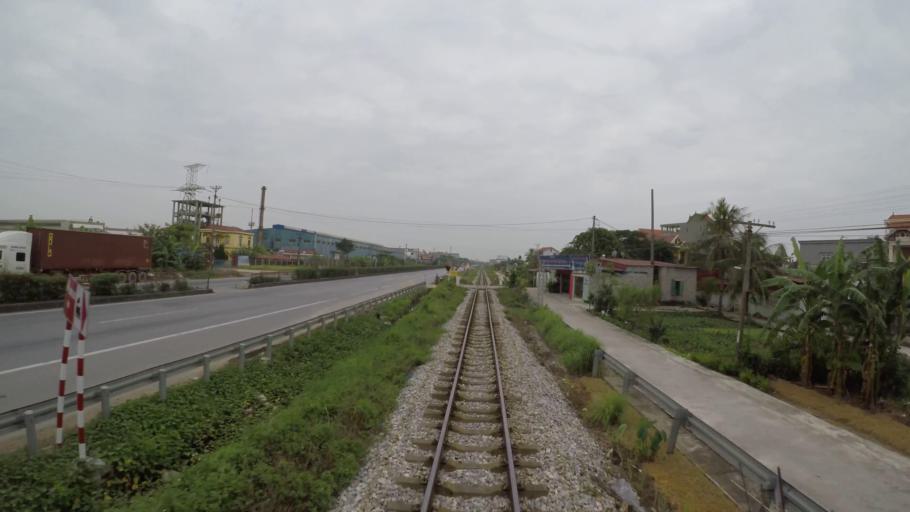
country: VN
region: Hai Duong
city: Phu Thai
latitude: 20.9468
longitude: 106.5382
